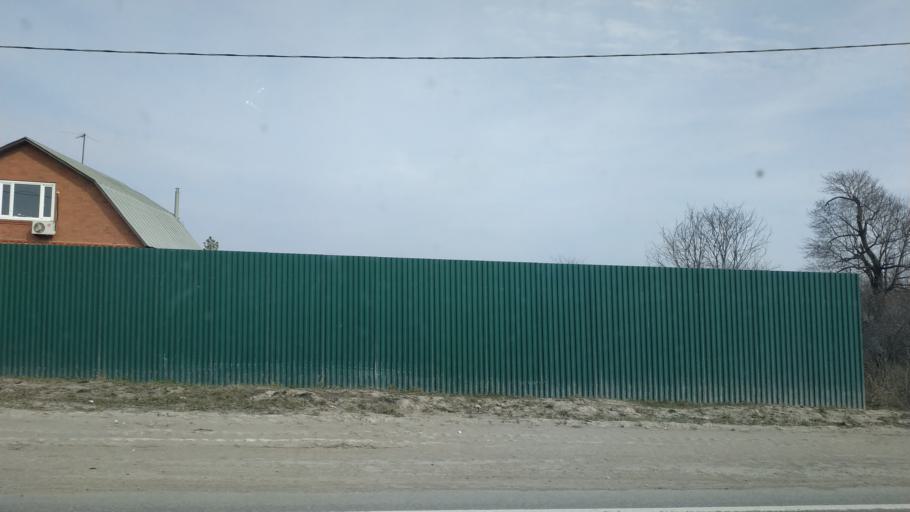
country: RU
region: Moskovskaya
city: Bronnitsy
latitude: 55.3937
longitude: 38.3235
